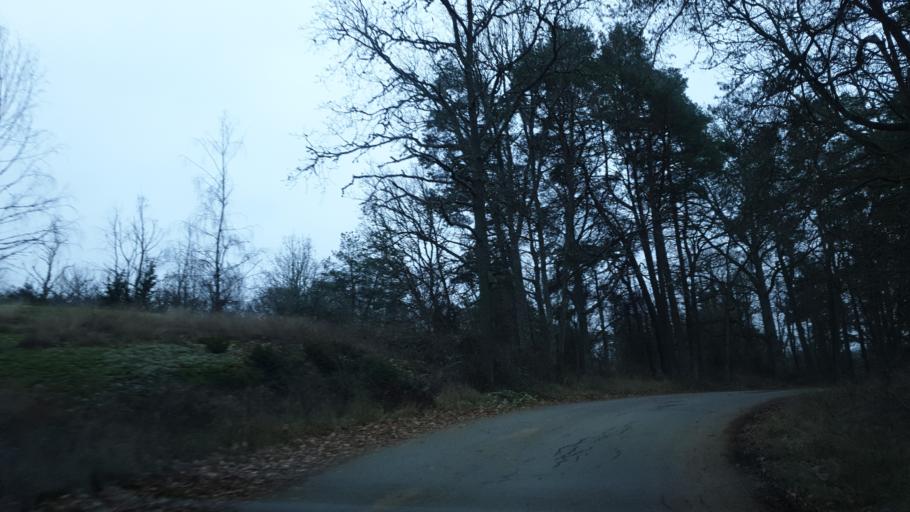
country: SE
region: Blekinge
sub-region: Karlskrona Kommun
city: Karlskrona
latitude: 56.1717
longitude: 15.5642
